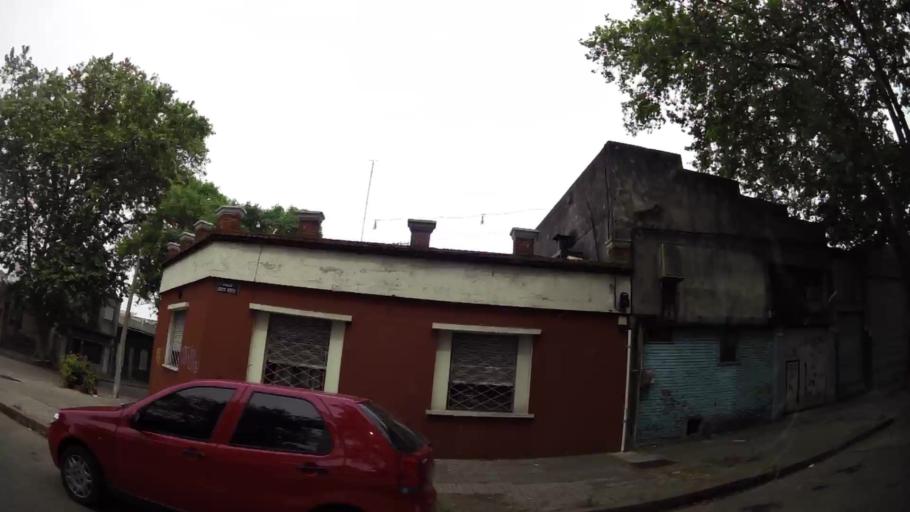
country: UY
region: Montevideo
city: Montevideo
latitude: -34.8910
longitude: -56.1719
